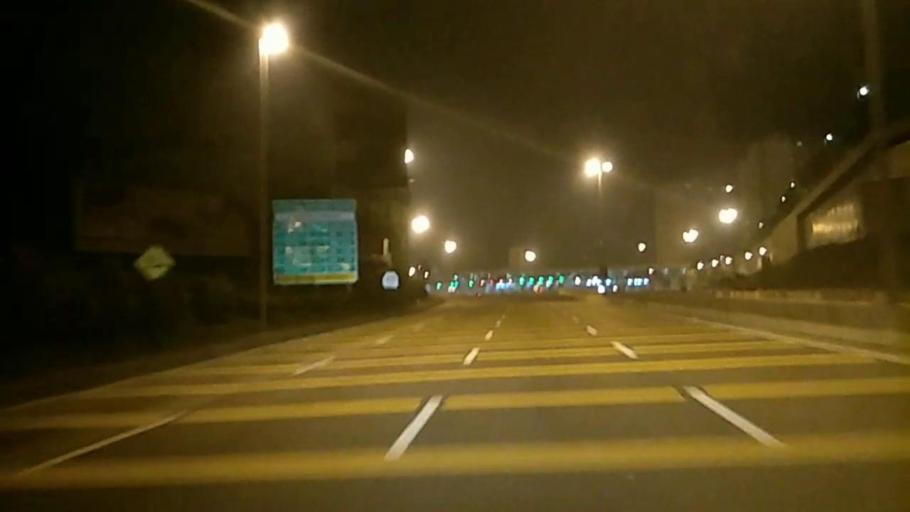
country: MY
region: Selangor
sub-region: Petaling
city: Petaling Jaya
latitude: 3.1815
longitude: 101.6192
